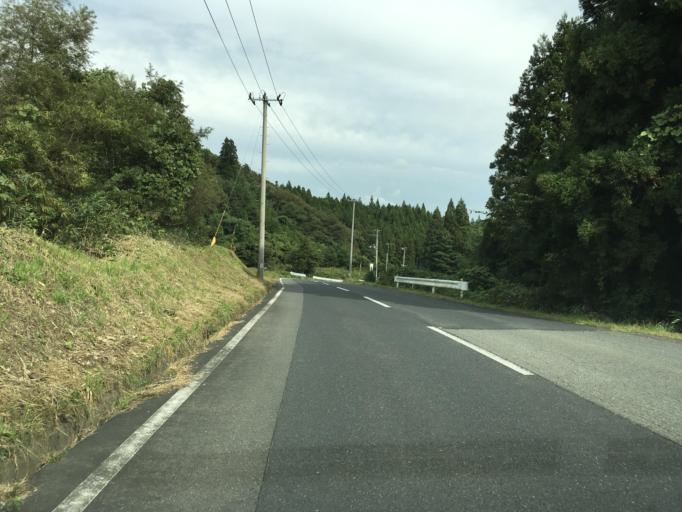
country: JP
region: Iwate
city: Mizusawa
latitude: 39.0392
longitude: 141.3179
